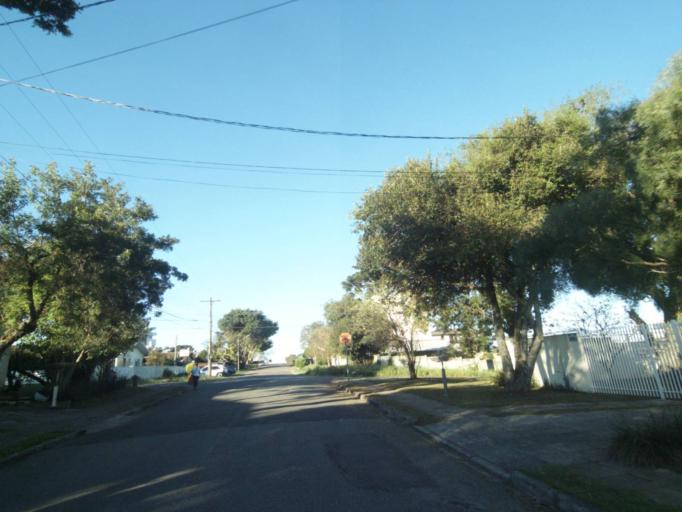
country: BR
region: Parana
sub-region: Curitiba
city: Curitiba
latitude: -25.3909
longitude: -49.2520
